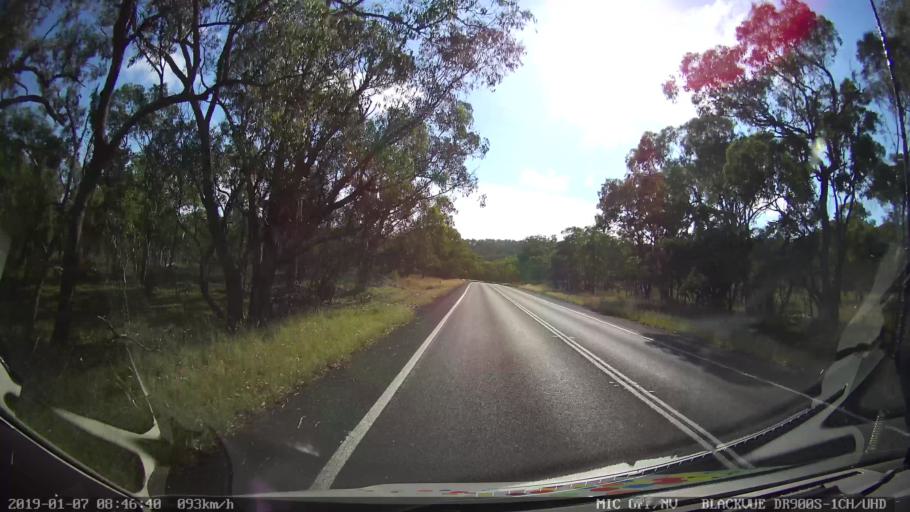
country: AU
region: New South Wales
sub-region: Tamworth Municipality
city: Kootingal
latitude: -30.8061
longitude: 151.2377
